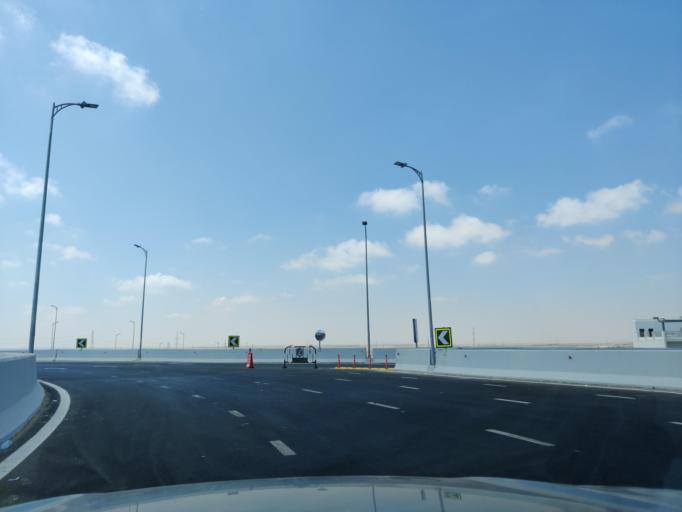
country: EG
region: Muhafazat Matruh
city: Al `Alamayn
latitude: 30.8241
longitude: 28.9854
